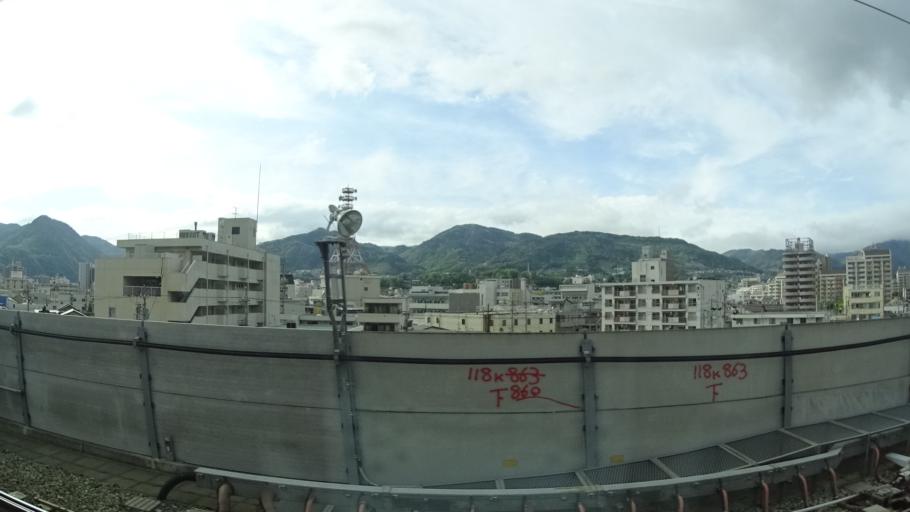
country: JP
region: Nagano
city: Nagano-shi
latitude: 36.6518
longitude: 138.2014
